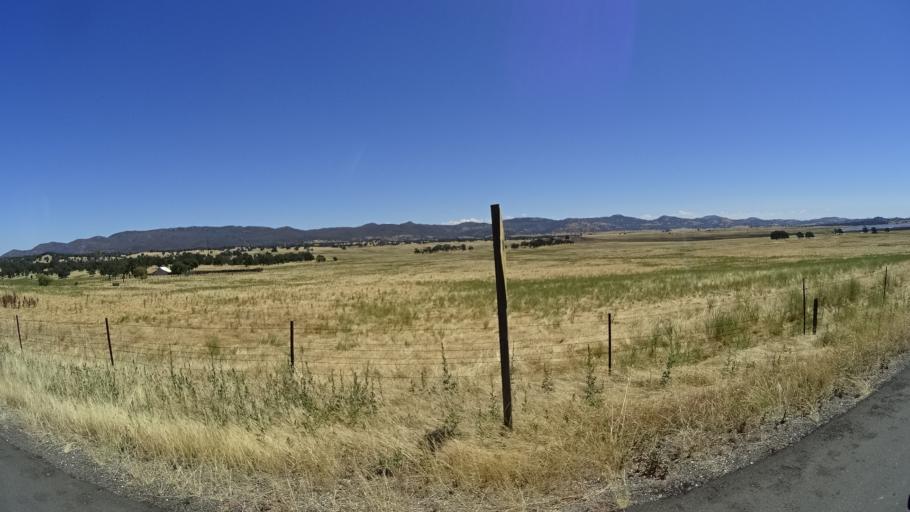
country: US
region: California
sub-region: Calaveras County
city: Rancho Calaveras
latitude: 38.0541
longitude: -120.7798
